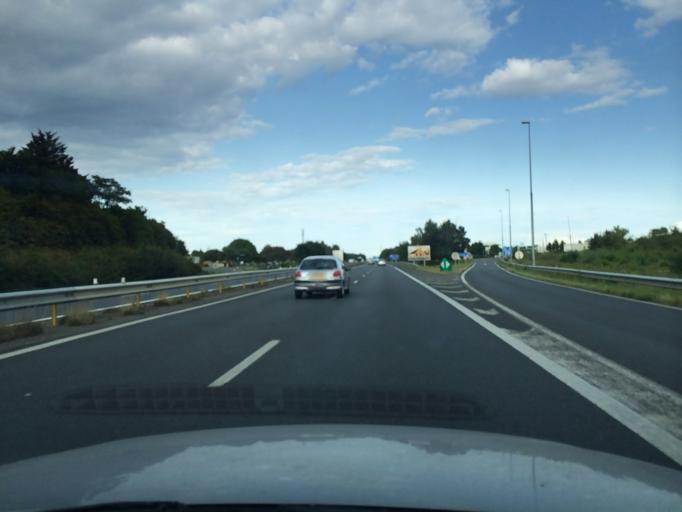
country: FR
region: Lower Normandy
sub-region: Departement du Calvados
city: Giberville
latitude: 49.1671
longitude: -0.2803
